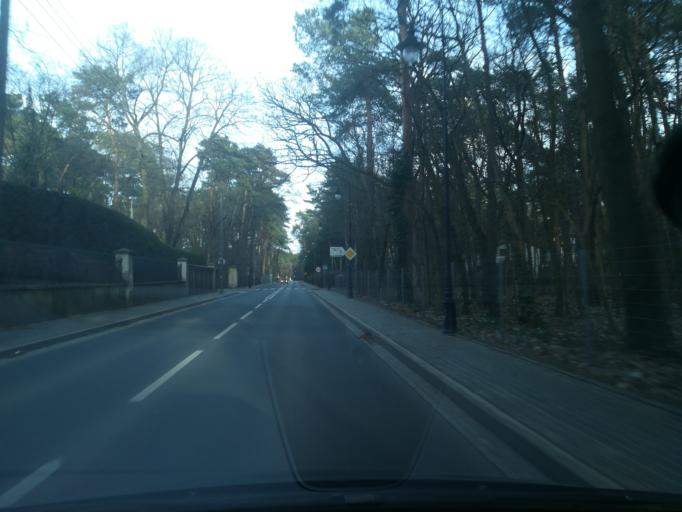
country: PL
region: Masovian Voivodeship
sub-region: Powiat piaseczynski
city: Konstancin-Jeziorna
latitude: 52.0775
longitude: 21.1064
